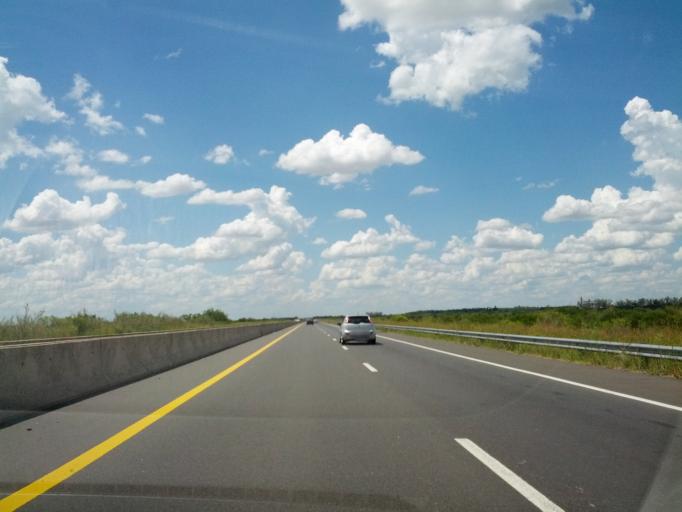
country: AR
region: Entre Rios
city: Colonia Elia
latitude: -32.7607
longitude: -58.4922
